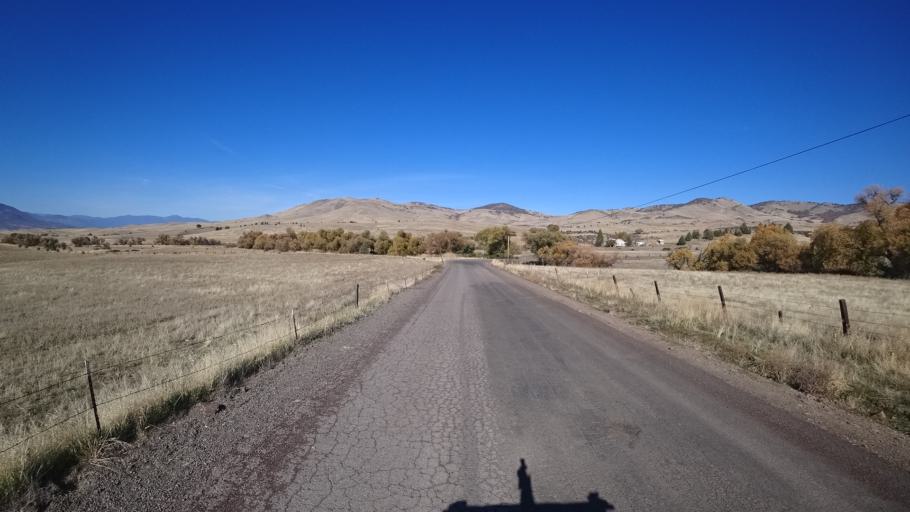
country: US
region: California
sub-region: Siskiyou County
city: Montague
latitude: 41.8141
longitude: -122.3767
